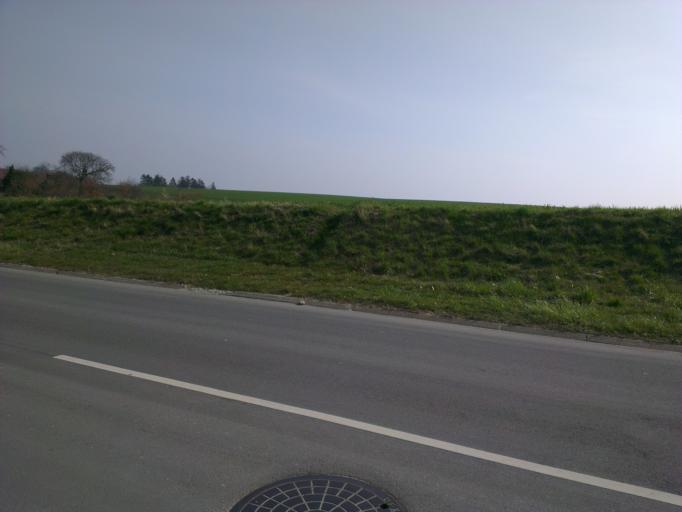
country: DK
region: Capital Region
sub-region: Frederikssund Kommune
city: Frederikssund
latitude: 55.8285
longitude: 12.0879
